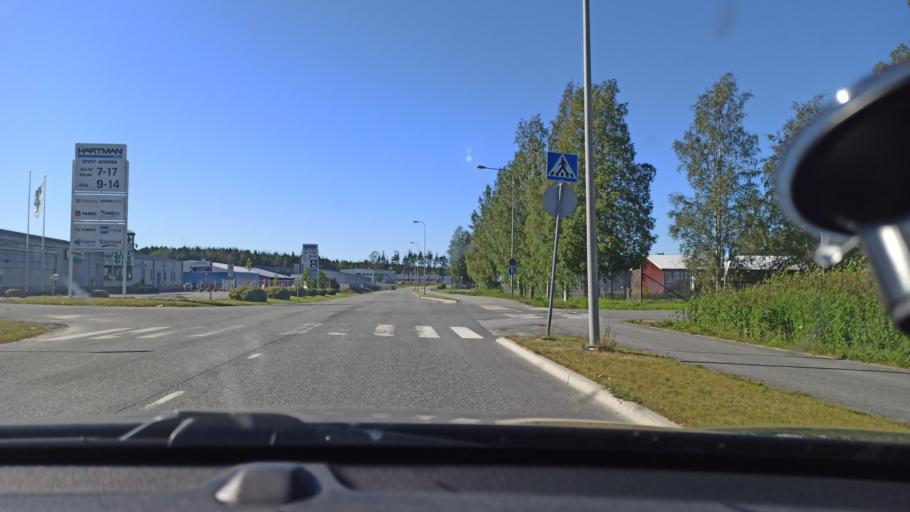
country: FI
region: Ostrobothnia
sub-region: Jakobstadsregionen
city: Jakobstad
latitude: 63.6872
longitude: 22.7086
